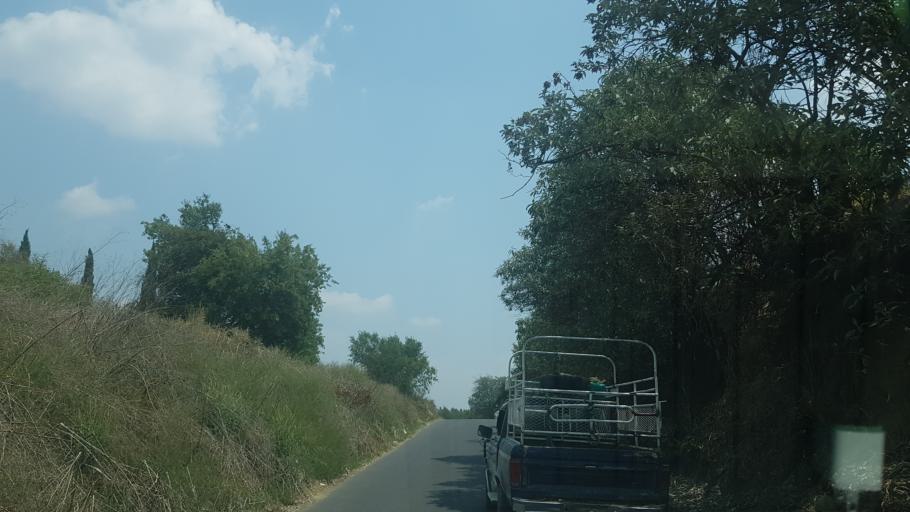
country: MX
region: Puebla
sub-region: San Nicolas de los Ranchos
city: San Pedro Yancuitlalpan
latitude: 19.0934
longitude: -98.4830
